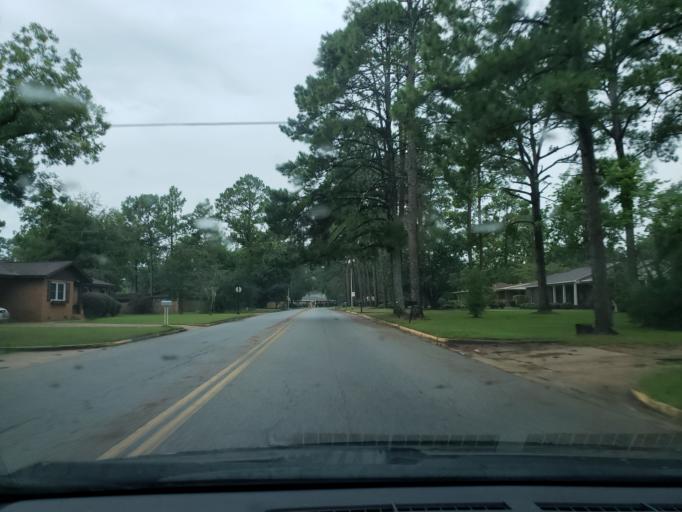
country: US
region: Georgia
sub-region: Dougherty County
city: Albany
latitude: 31.6050
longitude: -84.1921
